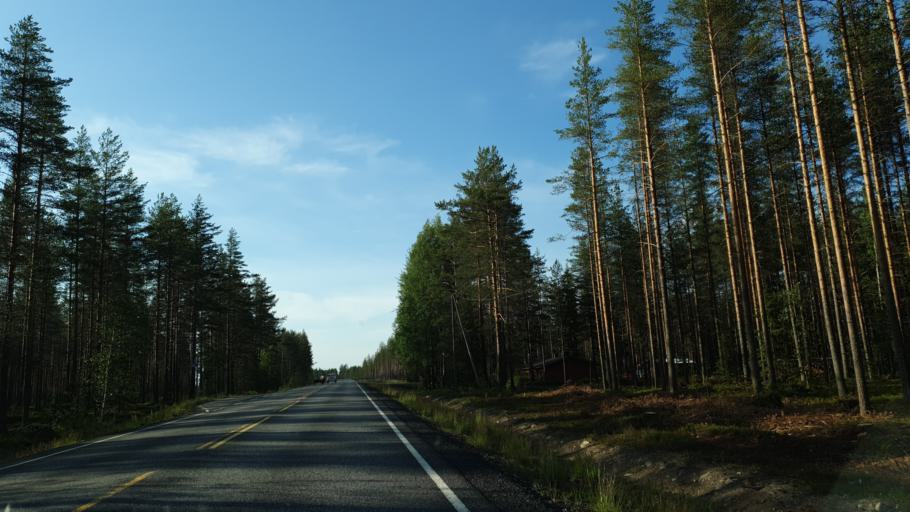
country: FI
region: Kainuu
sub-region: Kehys-Kainuu
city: Kuhmo
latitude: 64.0878
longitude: 29.4824
